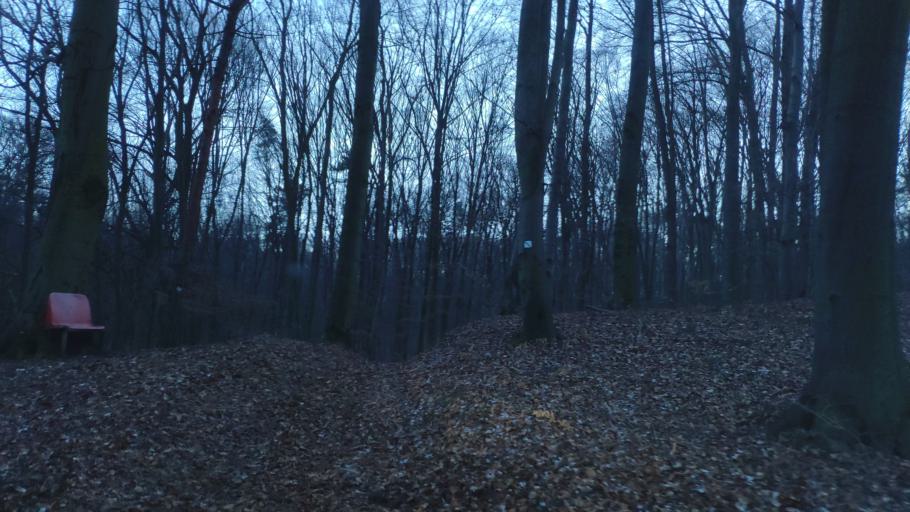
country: SK
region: Kosicky
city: Kosice
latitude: 48.8431
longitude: 21.2461
